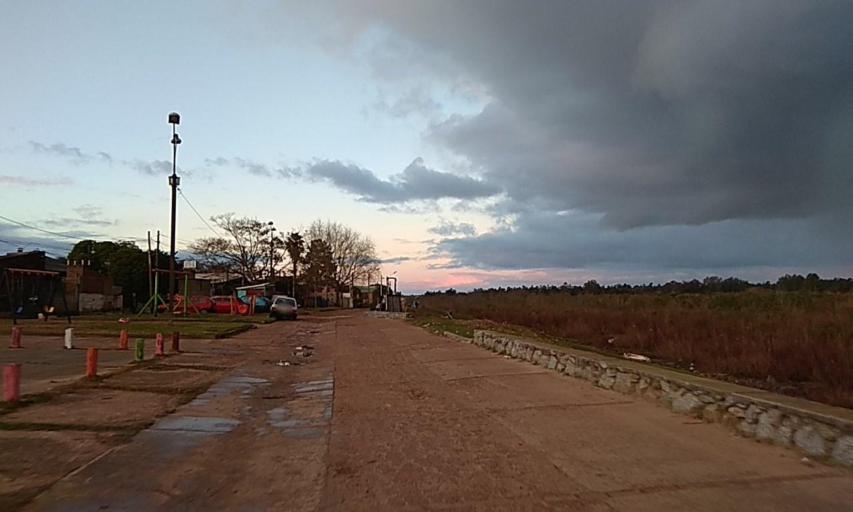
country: UY
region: Florida
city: Florida
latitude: -34.1102
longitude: -56.2086
